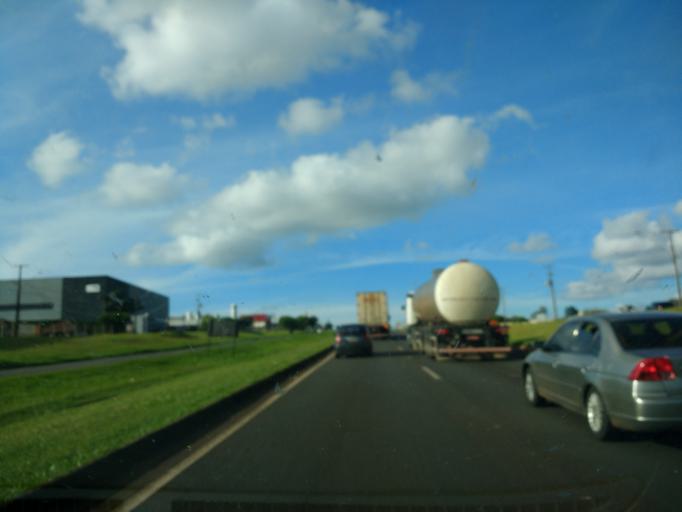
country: BR
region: Parana
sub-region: Cambe
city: Cambe
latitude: -23.2930
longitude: -51.2675
